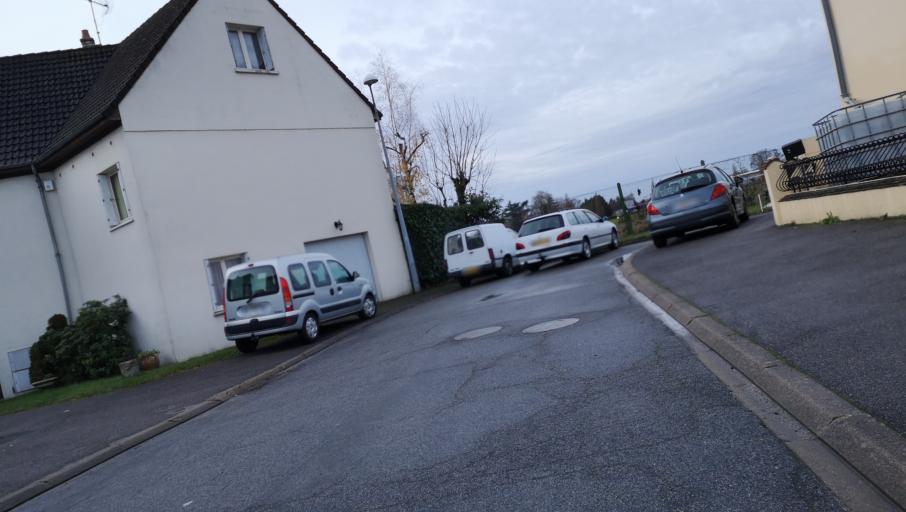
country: FR
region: Centre
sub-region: Departement du Loiret
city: Saint-Jean-de-Braye
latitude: 47.9205
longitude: 1.9634
